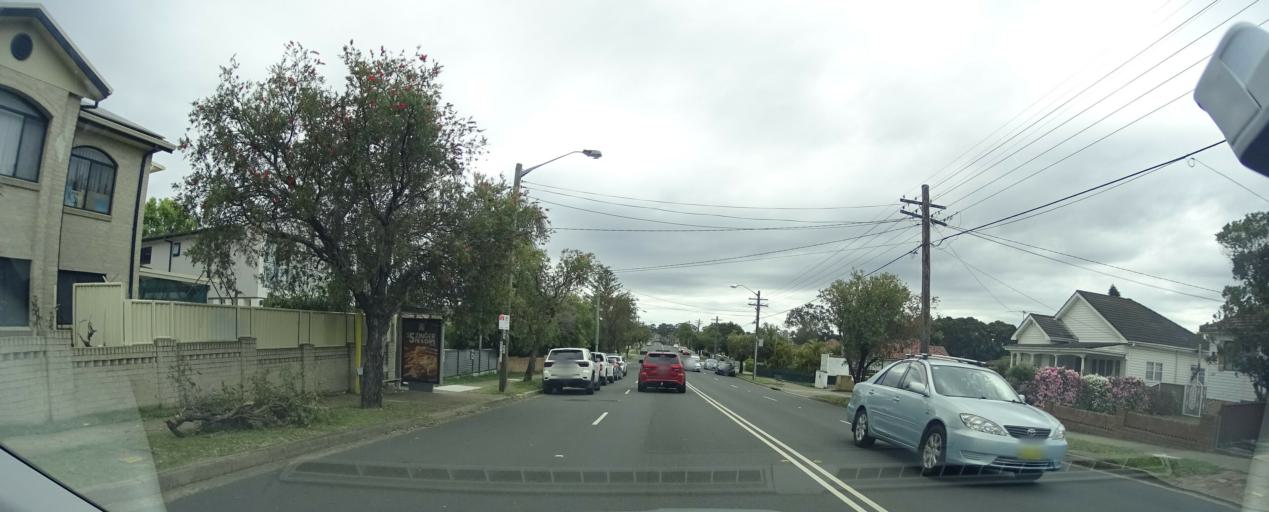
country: AU
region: New South Wales
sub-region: Bankstown
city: Revesby
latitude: -33.9583
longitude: 151.0166
